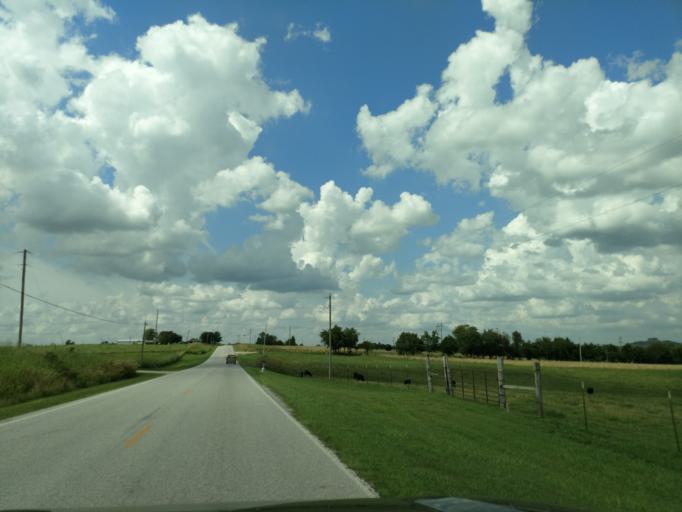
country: US
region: Arkansas
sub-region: Carroll County
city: Berryville
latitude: 36.4530
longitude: -93.5560
